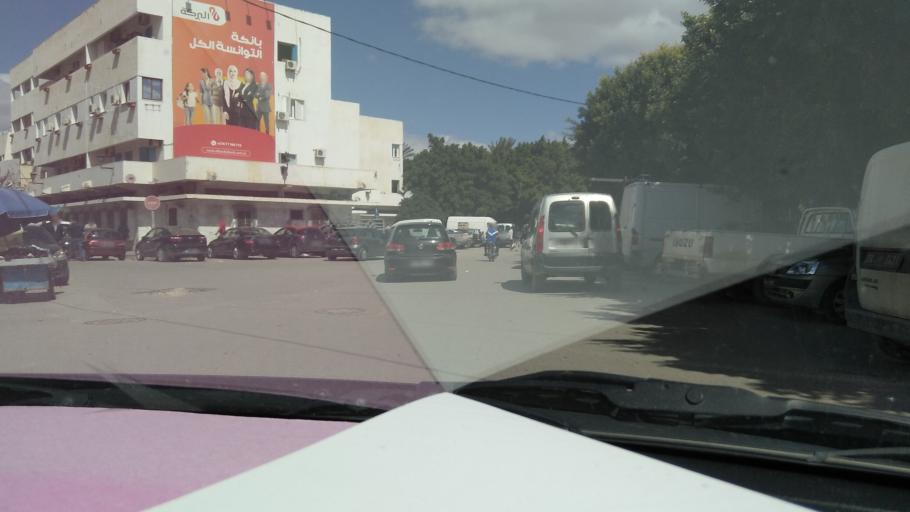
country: TN
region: Al Qayrawan
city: Kairouan
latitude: 35.6715
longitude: 10.1029
